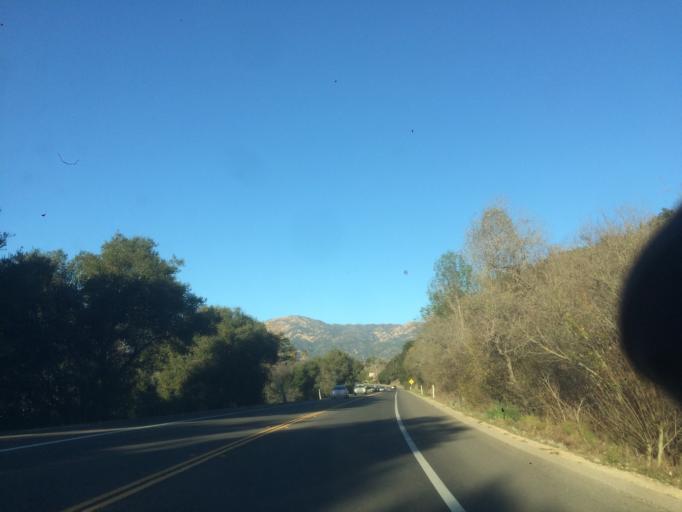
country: US
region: California
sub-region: Santa Barbara County
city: Mission Canyon
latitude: 34.4200
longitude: -119.7405
